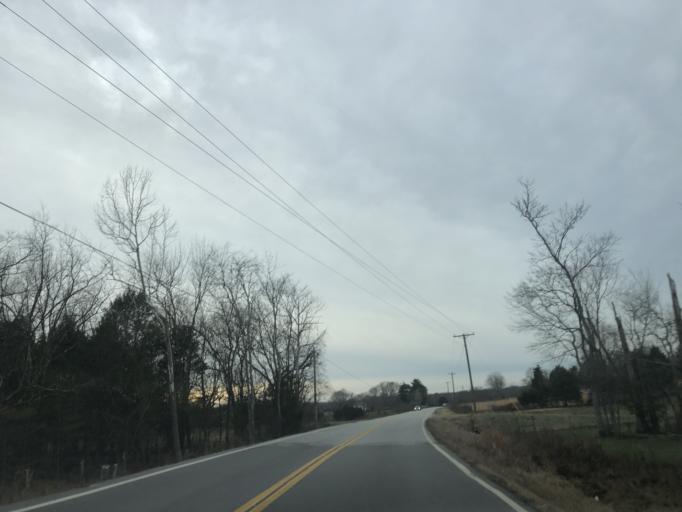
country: US
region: Tennessee
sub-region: Wilson County
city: Rural Hill
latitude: 36.1261
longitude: -86.3789
